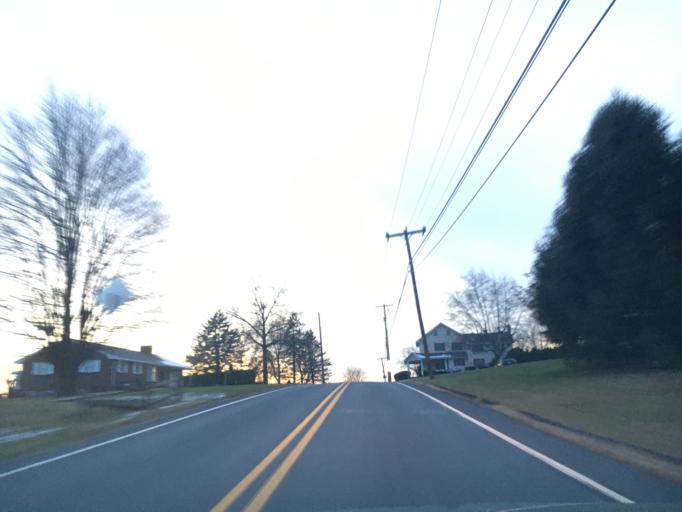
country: US
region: Pennsylvania
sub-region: Northampton County
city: Youngsville
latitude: 40.7599
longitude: -75.4617
